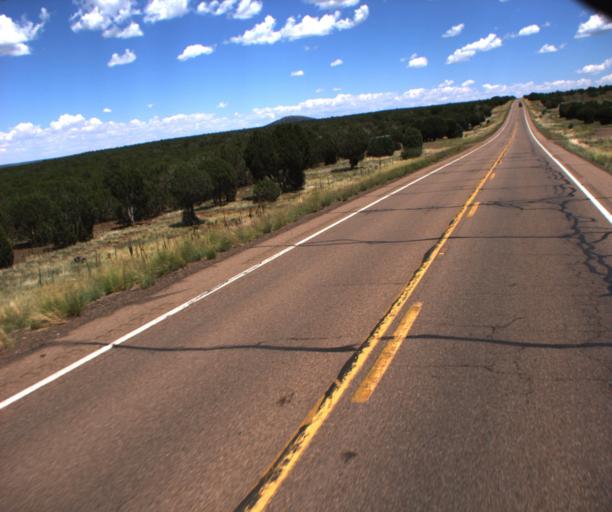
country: US
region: Arizona
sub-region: Navajo County
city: White Mountain Lake
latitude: 34.2715
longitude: -109.9196
